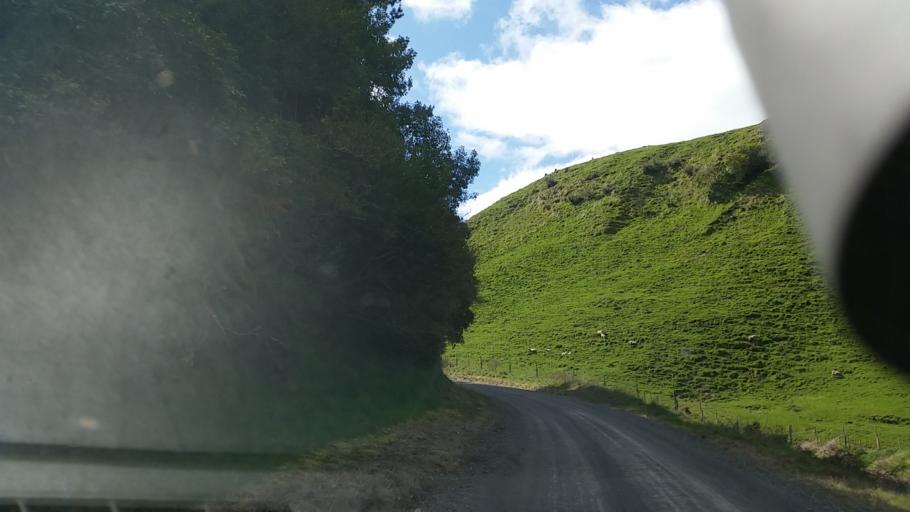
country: NZ
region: Waikato
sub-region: Taupo District
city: Taupo
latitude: -38.4900
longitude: 176.2089
